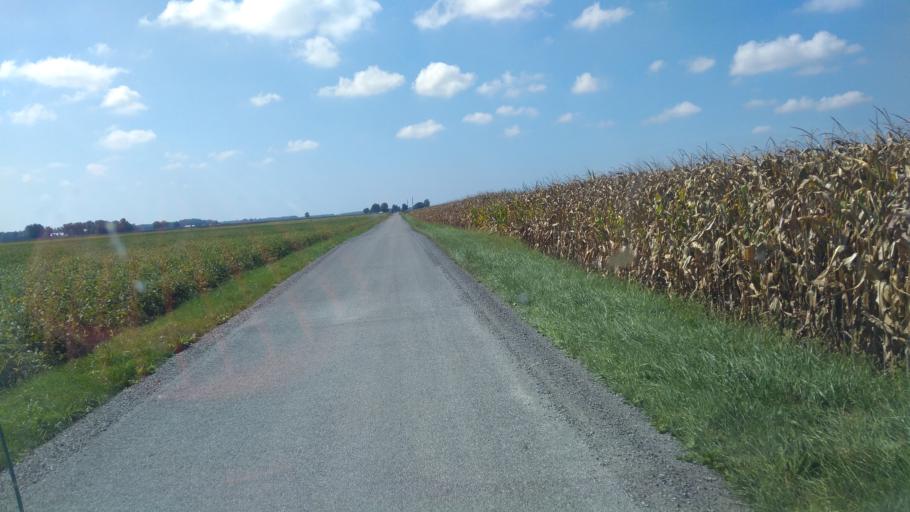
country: US
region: Ohio
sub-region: Hardin County
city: Ada
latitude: 40.7618
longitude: -83.7347
